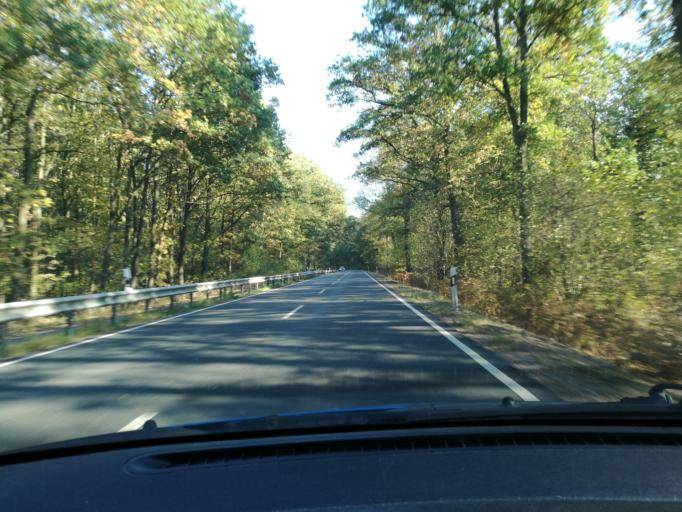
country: DE
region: Lower Saxony
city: Damnatz
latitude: 53.1017
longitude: 11.1576
